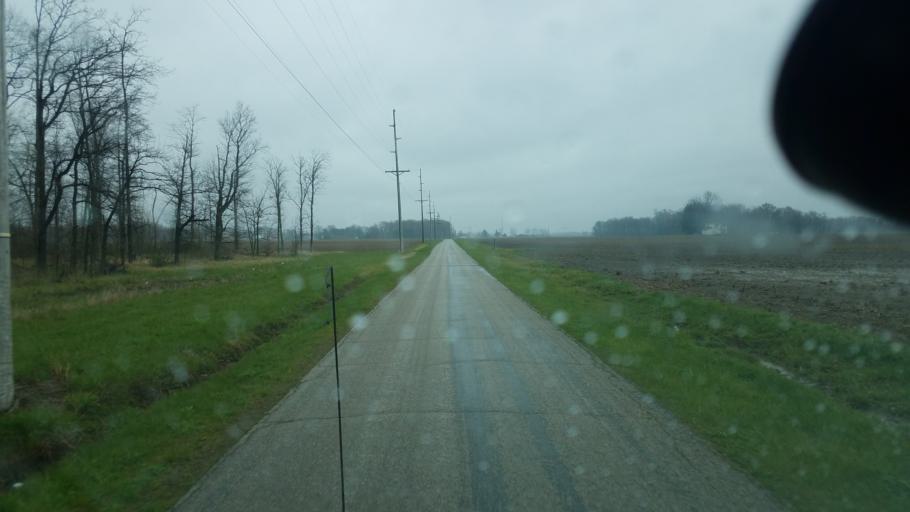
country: US
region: Ohio
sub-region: Crawford County
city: Bucyrus
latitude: 40.8339
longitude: -83.0804
